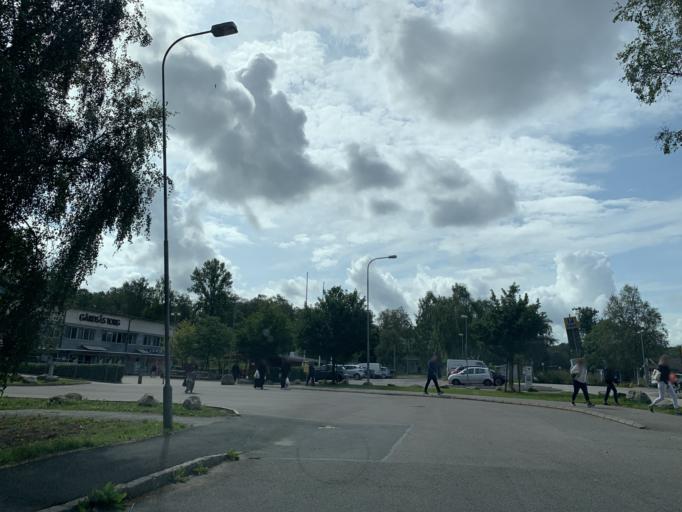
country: SE
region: Vaestra Goetaland
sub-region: Goteborg
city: Eriksbo
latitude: 57.7614
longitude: 12.0520
